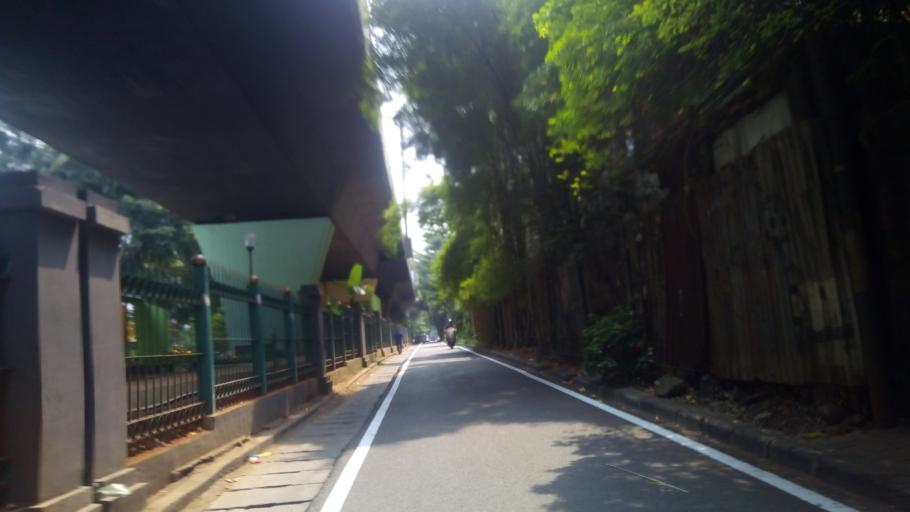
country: ID
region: Jakarta Raya
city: Jakarta
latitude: -6.1949
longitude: 106.8387
